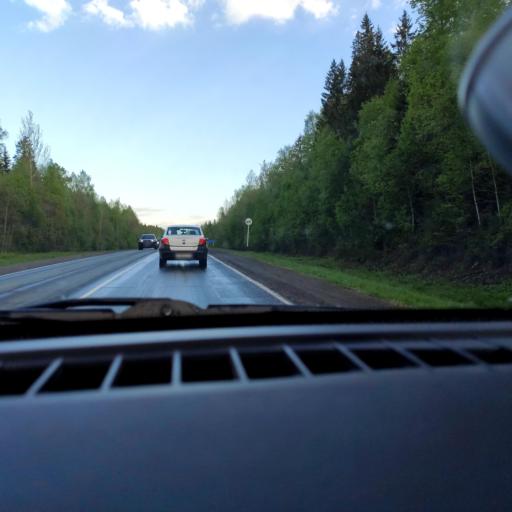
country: RU
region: Perm
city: Perm
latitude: 58.1607
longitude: 56.2457
